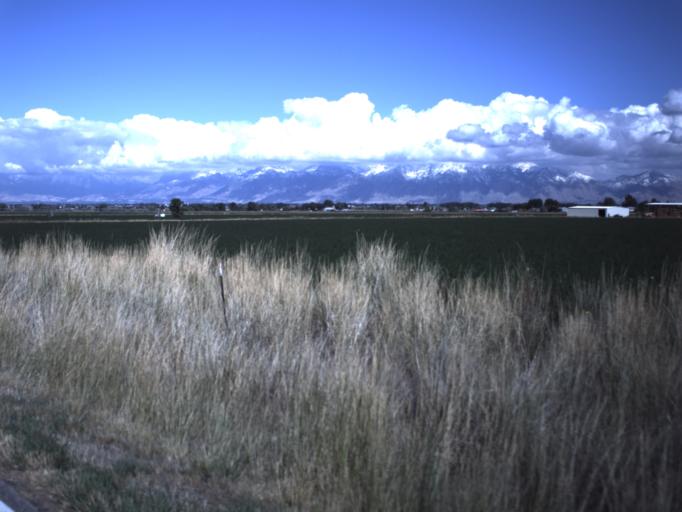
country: US
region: Utah
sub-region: Utah County
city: West Mountain
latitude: 40.0427
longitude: -111.7872
